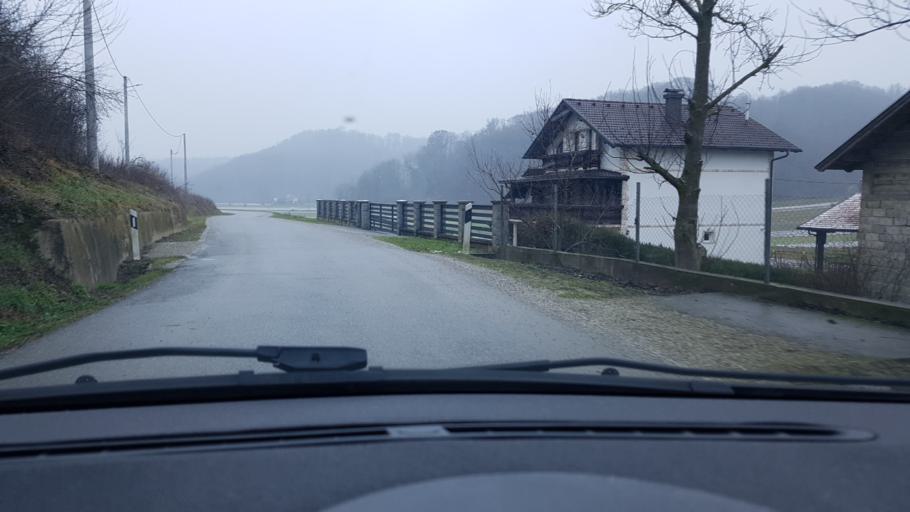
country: HR
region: Krapinsko-Zagorska
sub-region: Grad Krapina
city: Krapina
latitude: 46.0917
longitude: 15.8820
